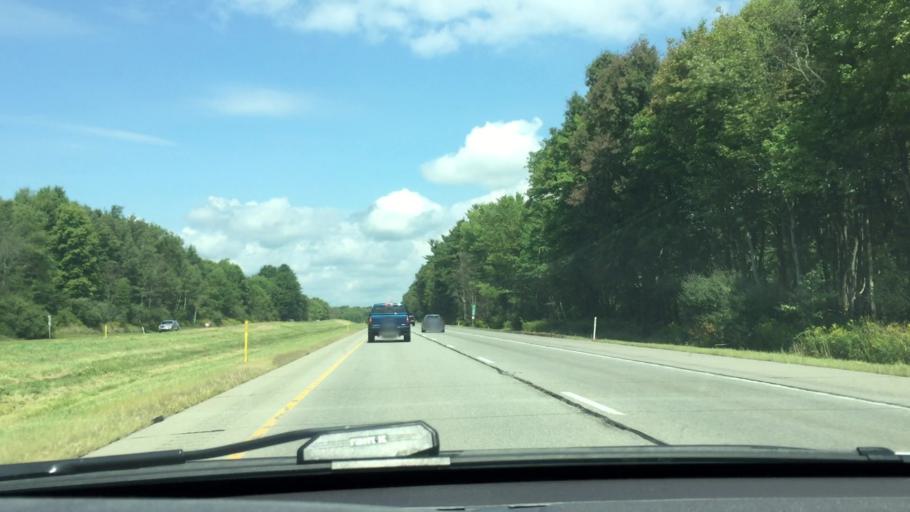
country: US
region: Pennsylvania
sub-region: Butler County
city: Slippery Rock
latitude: 41.0797
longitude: -80.1315
